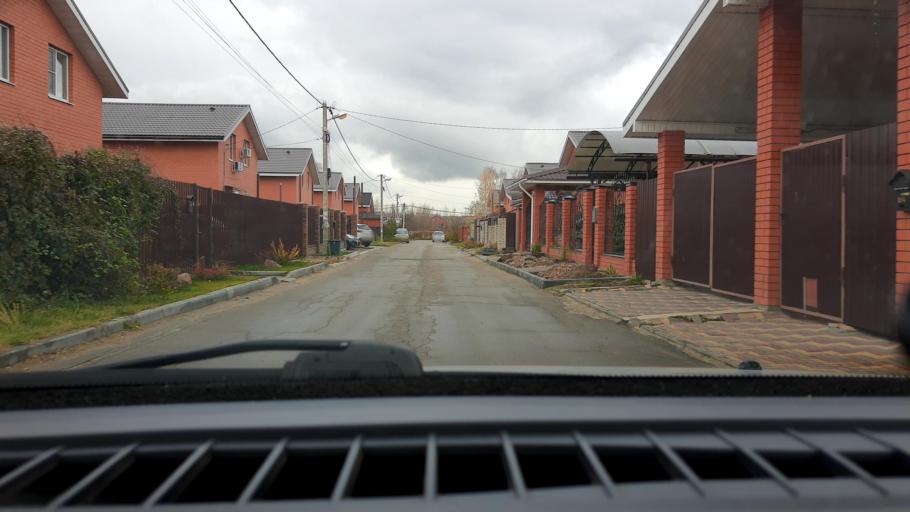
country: RU
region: Nizjnij Novgorod
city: Afonino
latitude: 56.2035
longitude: 44.1254
